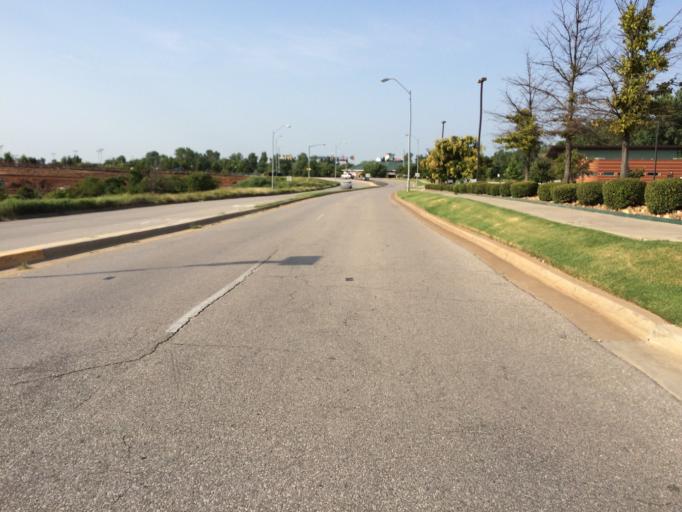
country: US
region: Oklahoma
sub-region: Cleveland County
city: Norman
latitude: 35.2057
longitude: -97.4828
